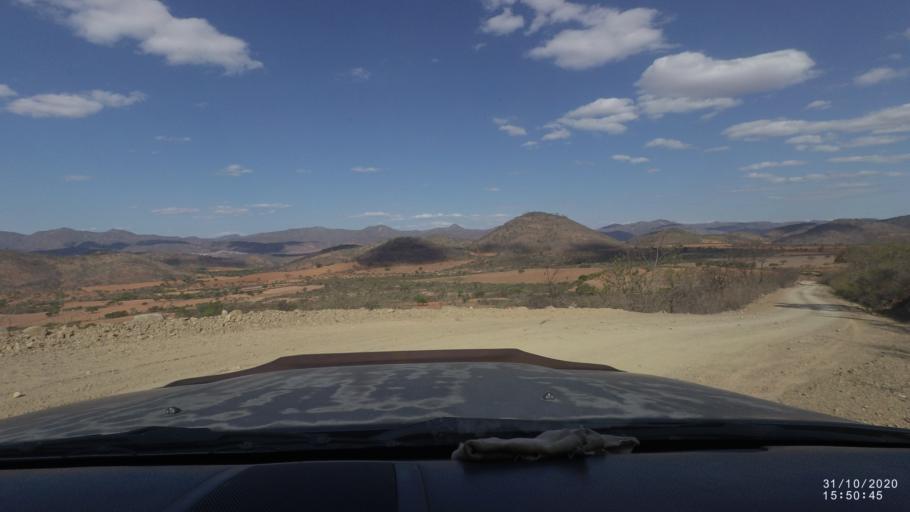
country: BO
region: Chuquisaca
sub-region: Provincia Zudanez
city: Mojocoya
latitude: -18.3132
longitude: -64.7047
